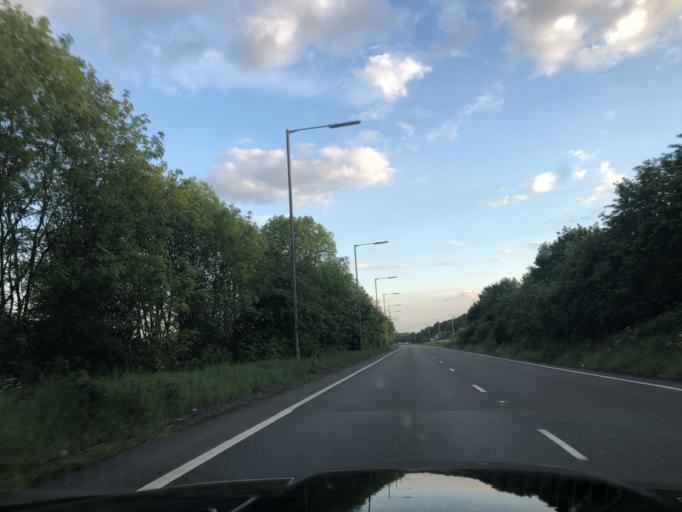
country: GB
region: England
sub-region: Warwickshire
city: Brandon
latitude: 52.4322
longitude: -1.4226
